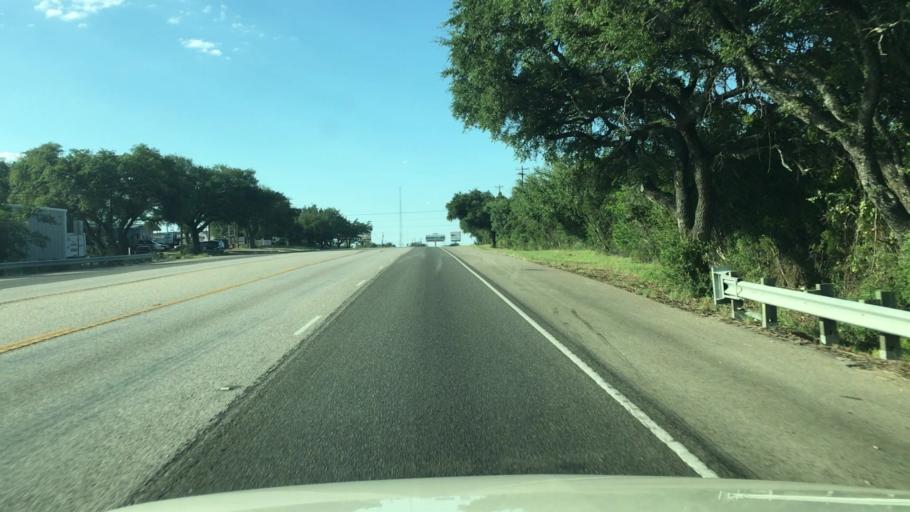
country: US
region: Texas
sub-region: Burnet County
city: Marble Falls
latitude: 30.6306
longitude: -98.2629
